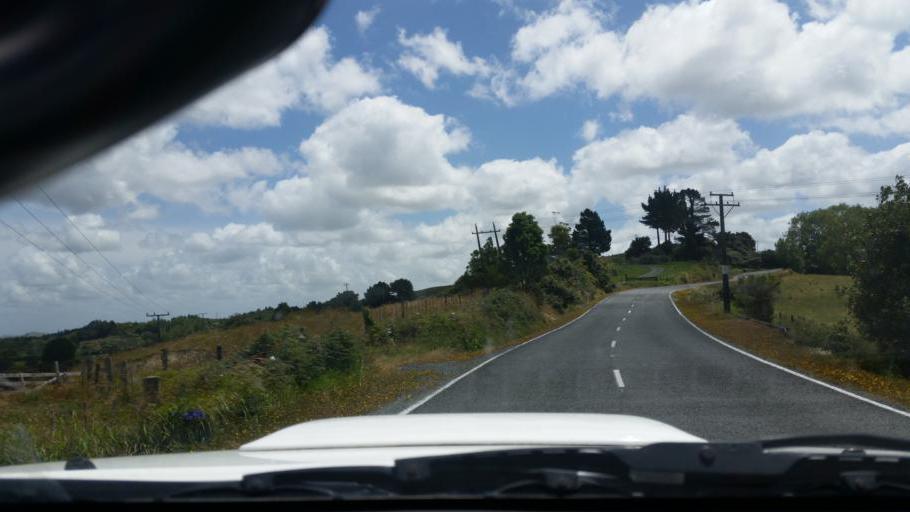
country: NZ
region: Northland
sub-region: Whangarei
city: Ruakaka
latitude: -36.0780
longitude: 174.2481
